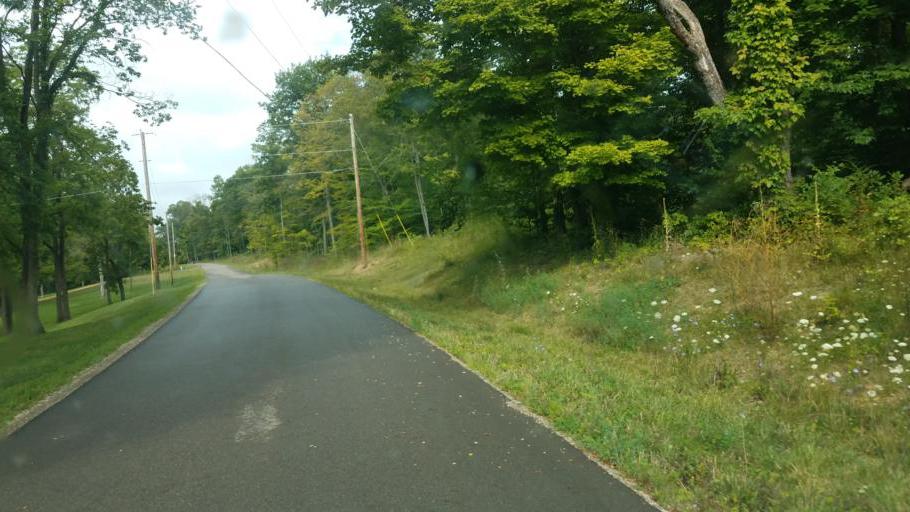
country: US
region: Ohio
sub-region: Morrow County
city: Cardington
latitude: 40.4325
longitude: -82.7945
